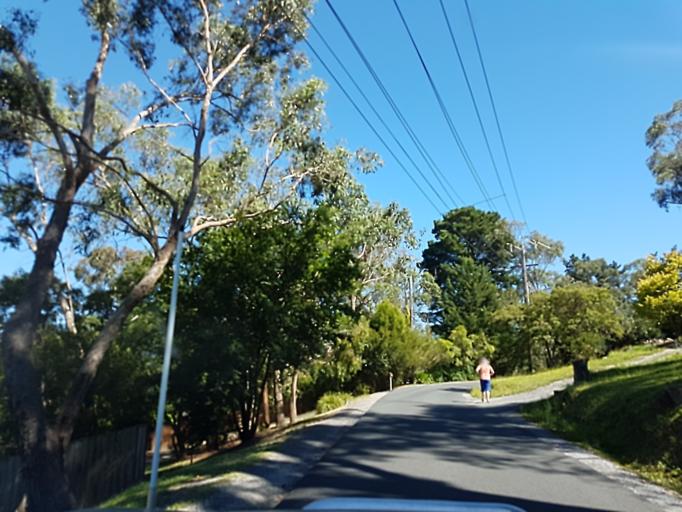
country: AU
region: Victoria
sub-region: Yarra Ranges
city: Tremont
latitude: -37.9148
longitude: 145.3241
